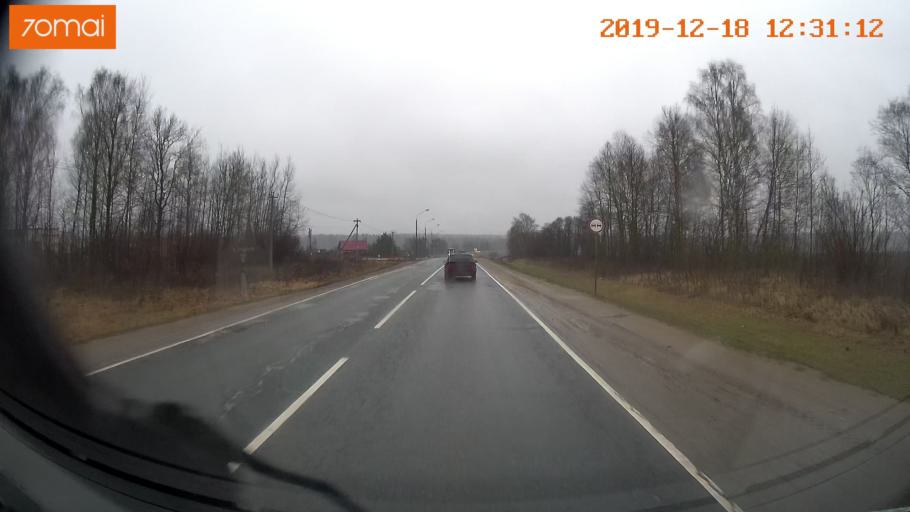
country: RU
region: Moskovskaya
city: Rumyantsevo
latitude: 56.0978
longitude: 36.5405
